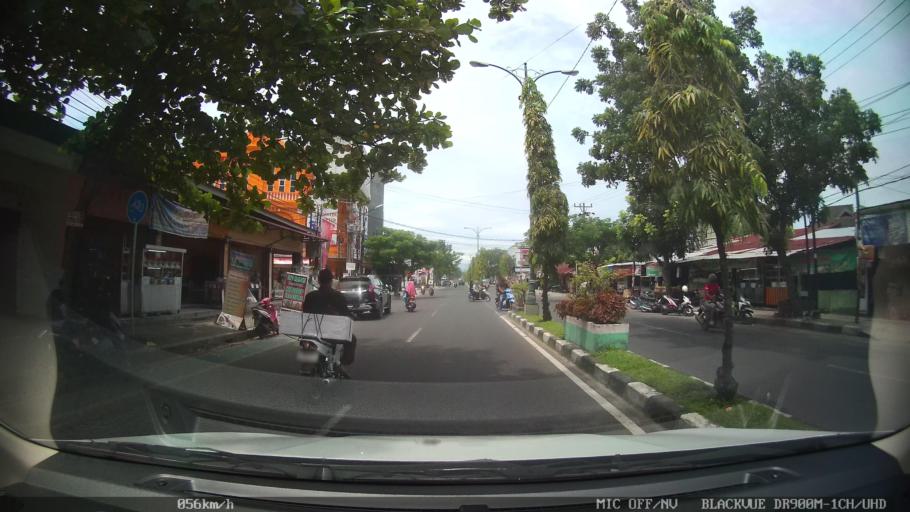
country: ID
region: North Sumatra
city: Sunggal
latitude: 3.5519
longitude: 98.6304
